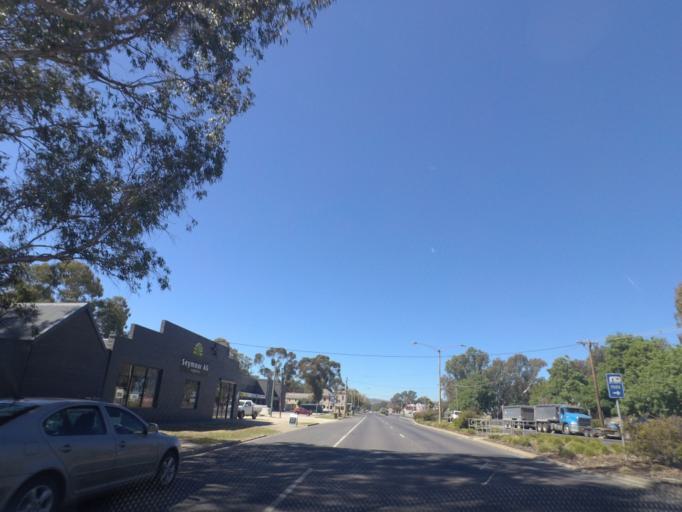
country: AU
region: Victoria
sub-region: Murrindindi
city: Kinglake West
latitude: -37.0212
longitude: 145.1251
